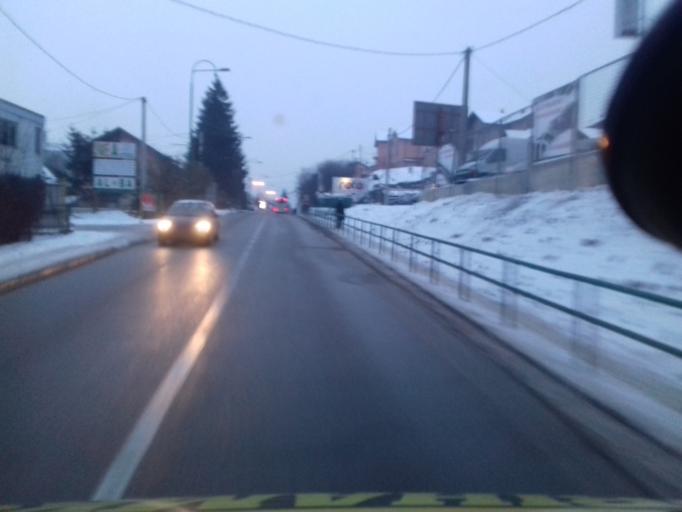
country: BA
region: Federation of Bosnia and Herzegovina
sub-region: Kanton Sarajevo
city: Sarajevo
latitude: 43.8558
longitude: 18.3248
